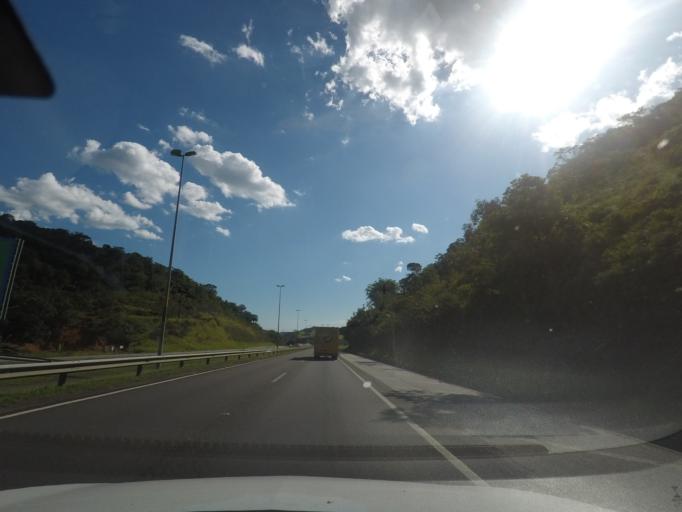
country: BR
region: Rio de Janeiro
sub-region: Guapimirim
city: Guapimirim
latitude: -22.5823
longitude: -43.0138
